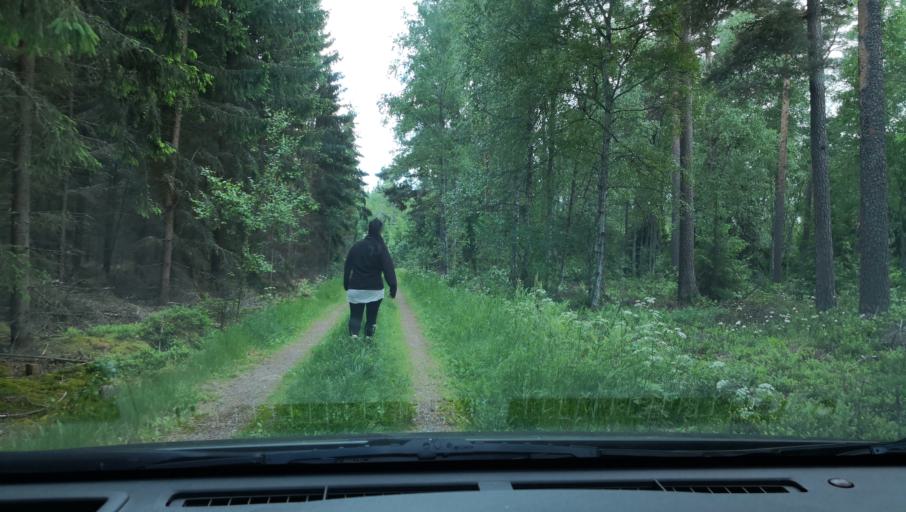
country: SE
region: OErebro
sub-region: Lindesbergs Kommun
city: Fellingsbro
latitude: 59.3048
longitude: 15.6676
